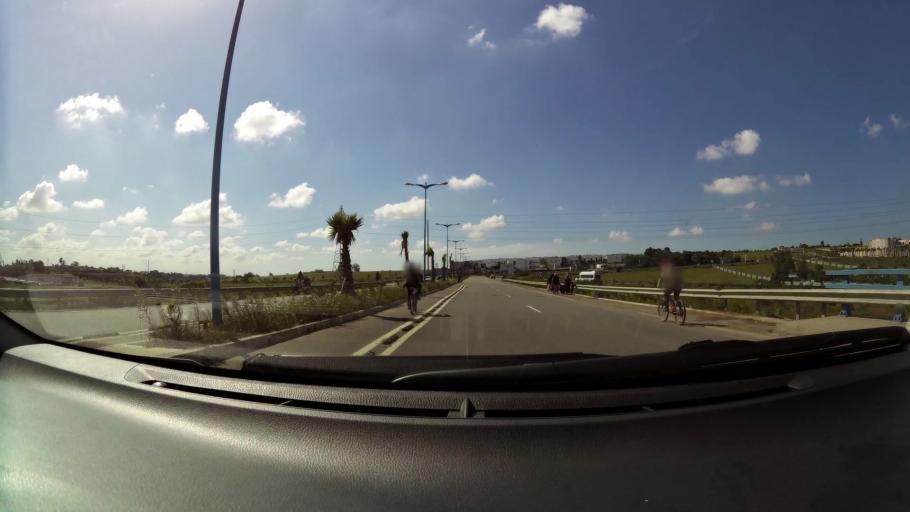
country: MA
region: Grand Casablanca
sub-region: Nouaceur
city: Bouskoura
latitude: 33.4833
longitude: -7.6328
